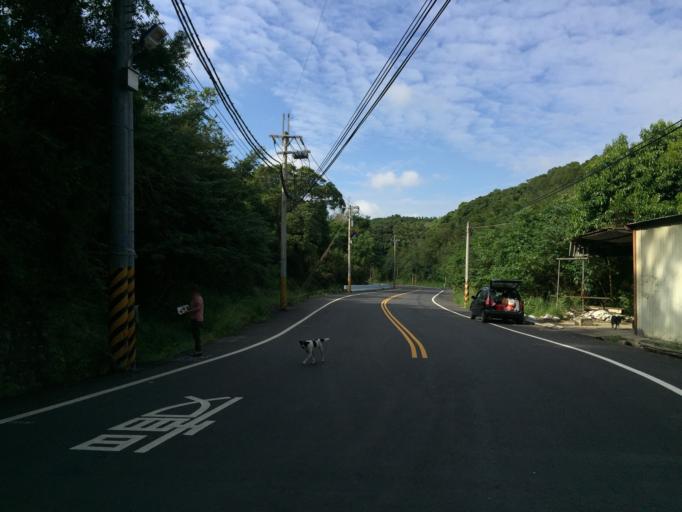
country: TW
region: Taiwan
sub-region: Hsinchu
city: Hsinchu
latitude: 24.7617
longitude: 120.9432
